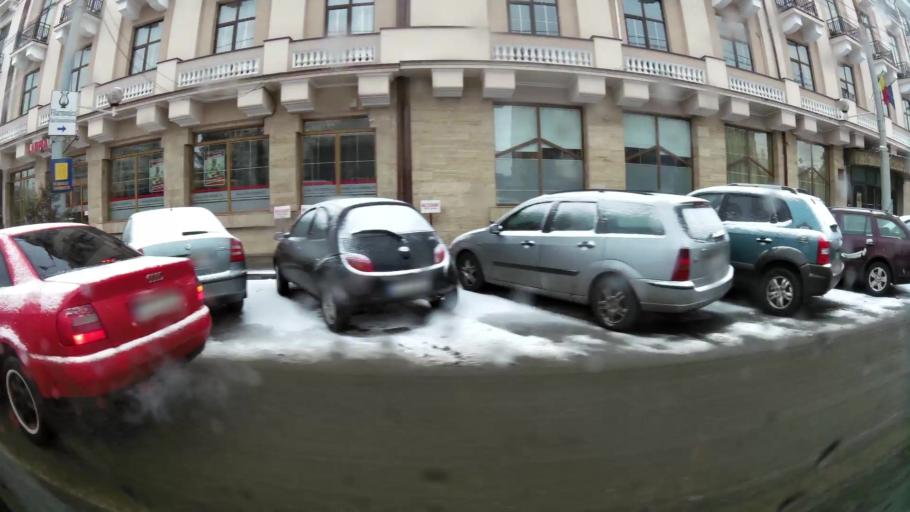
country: RO
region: Prahova
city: Ploiesti
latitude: 44.9406
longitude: 26.0232
